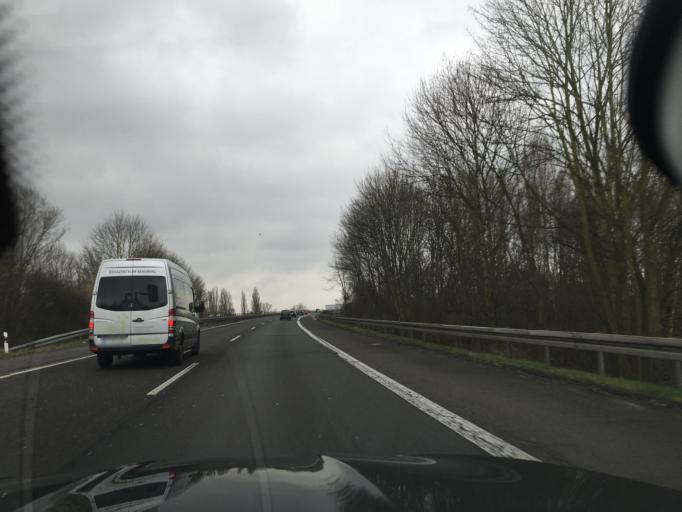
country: DE
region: North Rhine-Westphalia
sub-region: Regierungsbezirk Koln
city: Gremberghoven
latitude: 50.9209
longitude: 7.0623
